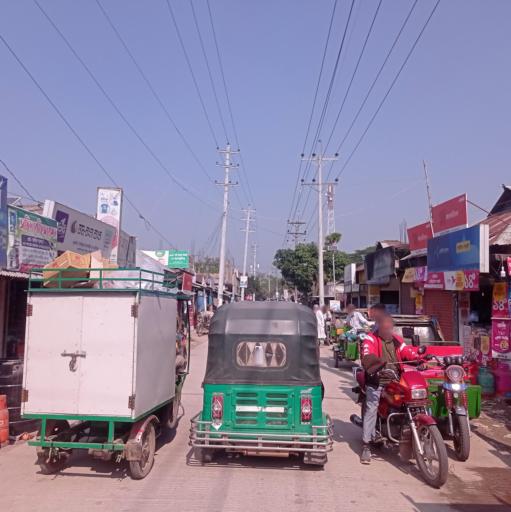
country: BD
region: Dhaka
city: Narsingdi
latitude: 24.0677
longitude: 90.6917
